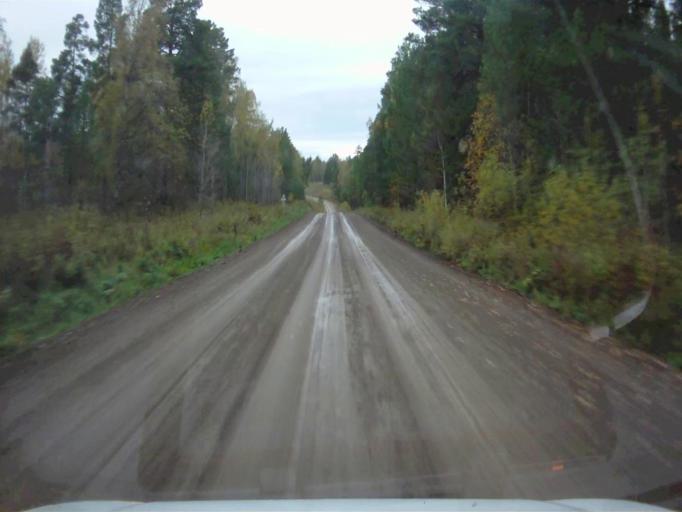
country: RU
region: Chelyabinsk
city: Nyazepetrovsk
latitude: 56.0882
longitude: 59.4163
